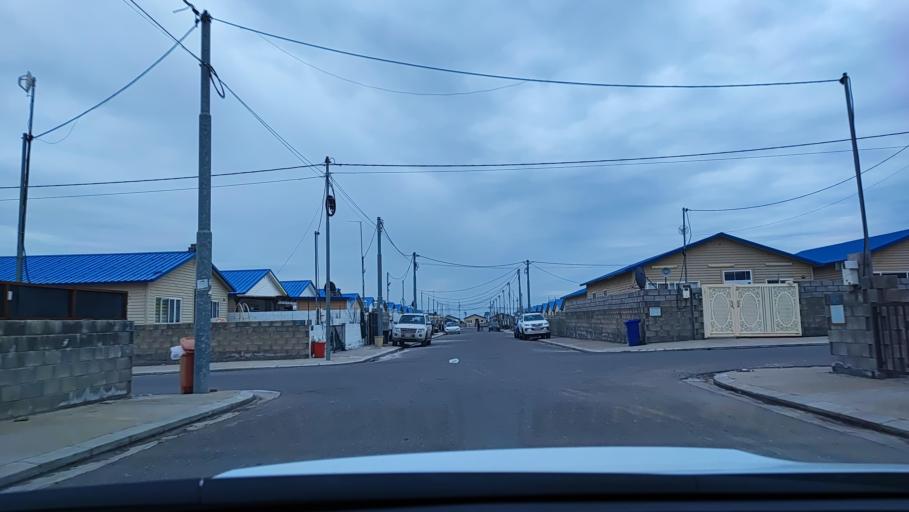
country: IQ
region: Arbil
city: Erbil
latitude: 36.2851
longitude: 44.0805
